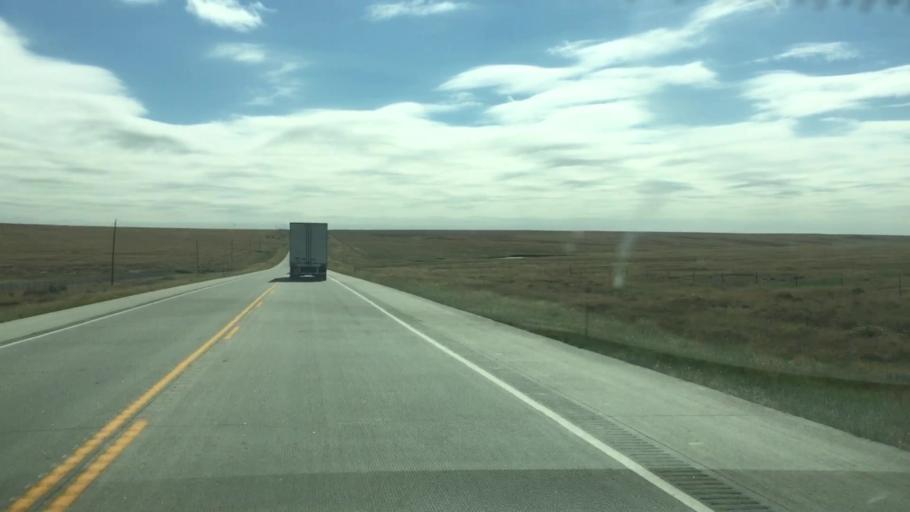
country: US
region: Colorado
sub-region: Lincoln County
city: Hugo
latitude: 39.0167
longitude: -103.3066
